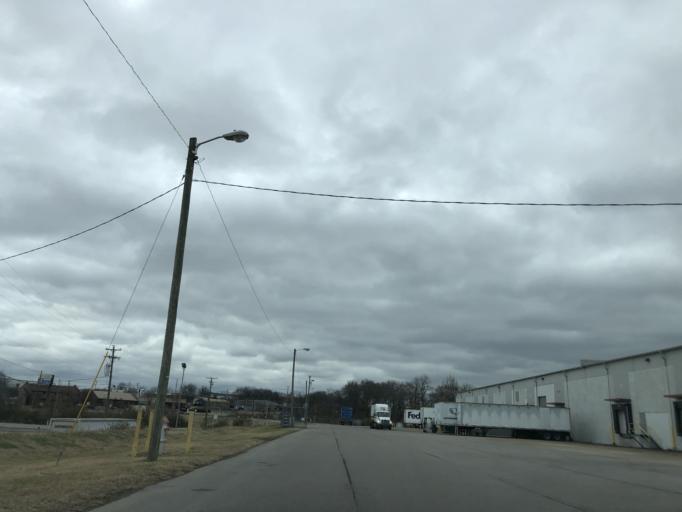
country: US
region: Tennessee
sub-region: Davidson County
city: Goodlettsville
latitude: 36.2834
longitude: -86.6953
